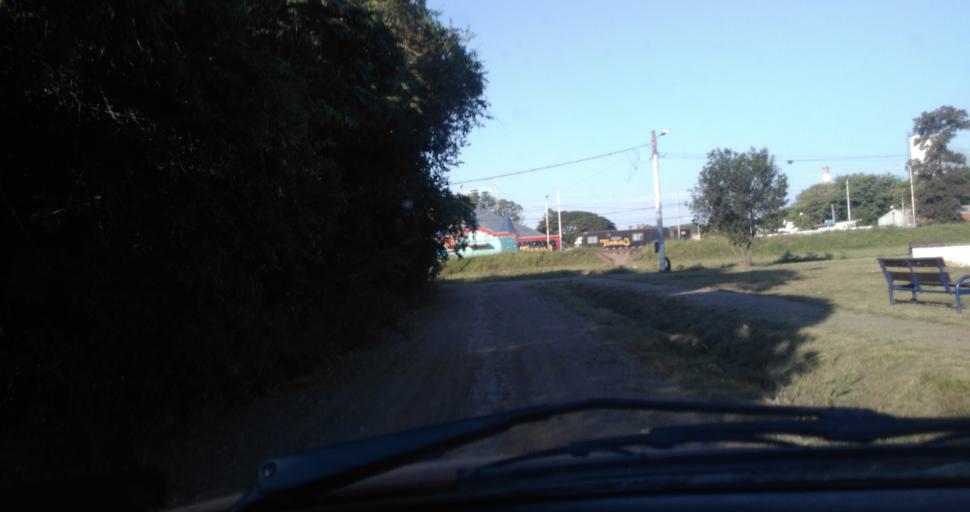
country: AR
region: Chaco
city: Fontana
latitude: -27.4199
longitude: -59.0377
